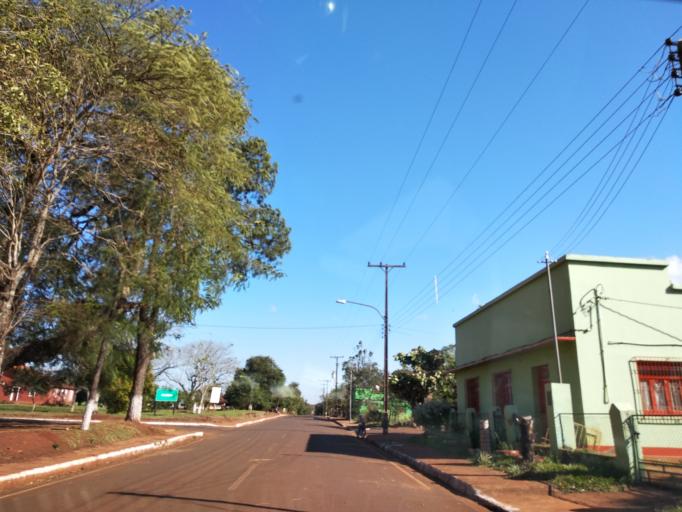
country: PY
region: Itapua
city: Hohenau
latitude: -27.0554
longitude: -55.7414
